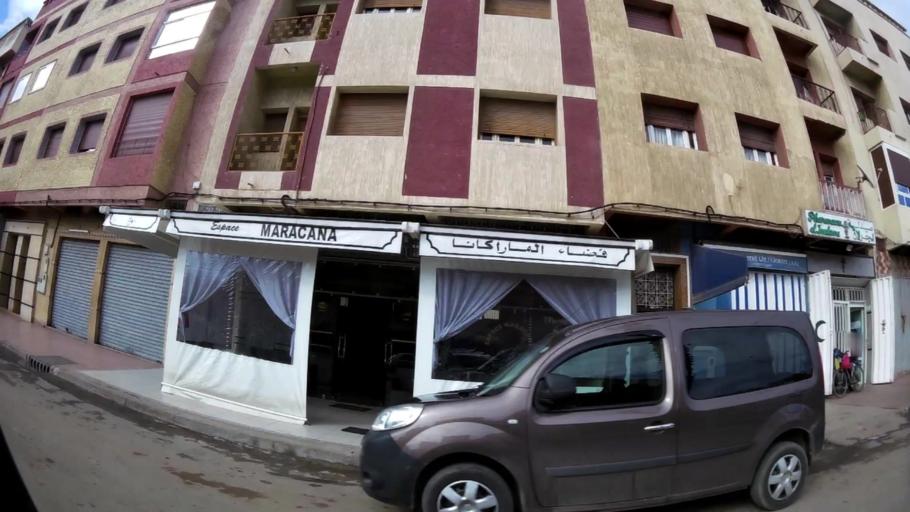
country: MA
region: Grand Casablanca
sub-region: Mohammedia
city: Mohammedia
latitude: 33.6879
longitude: -7.3774
